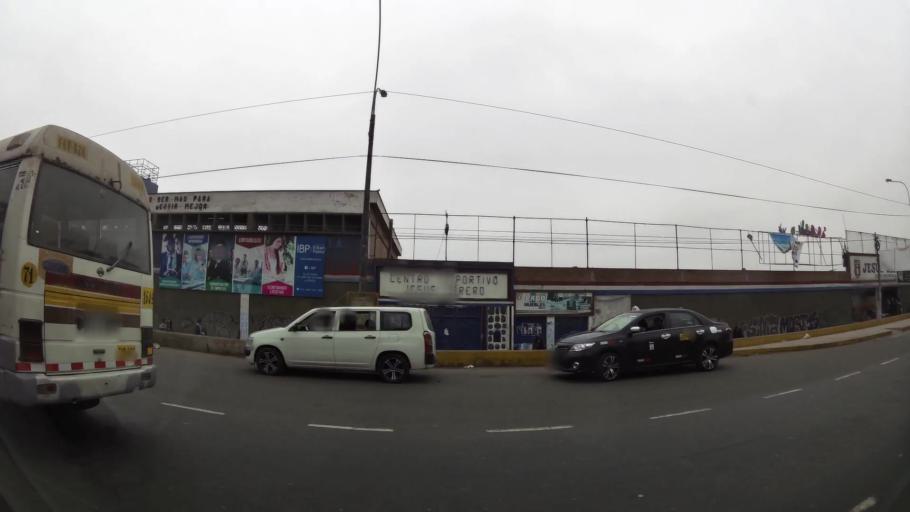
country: PE
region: Lima
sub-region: Lima
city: Independencia
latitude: -11.9532
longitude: -77.0515
